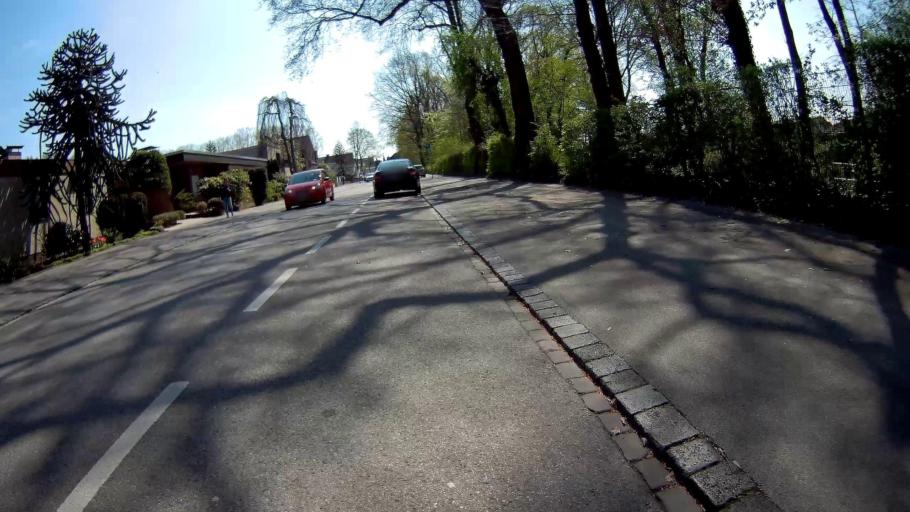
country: DE
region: North Rhine-Westphalia
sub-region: Regierungsbezirk Munster
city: Gladbeck
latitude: 51.5783
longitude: 7.0380
